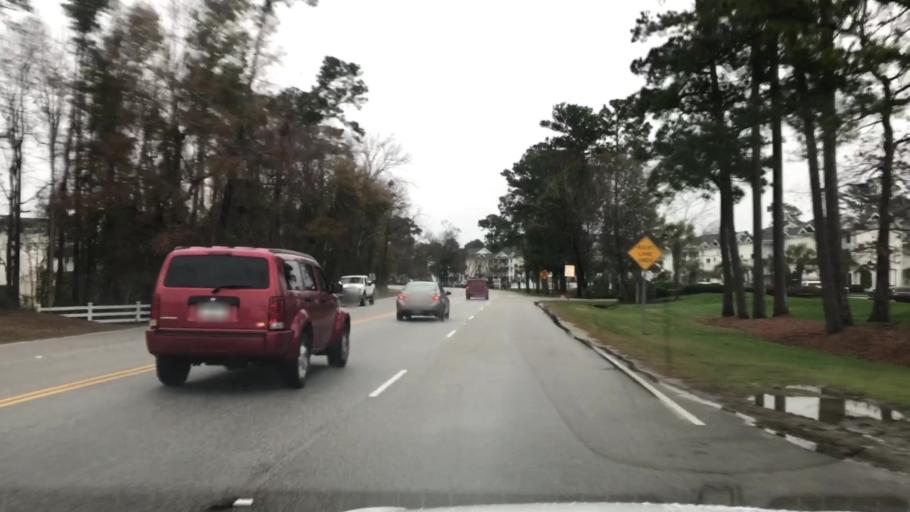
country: US
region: South Carolina
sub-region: Horry County
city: Forestbrook
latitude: 33.7224
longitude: -78.9210
